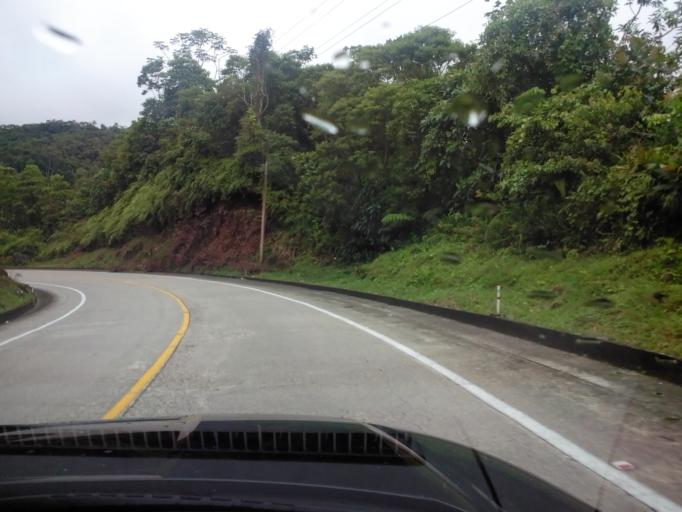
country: EC
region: Napo
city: Archidona
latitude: -0.7832
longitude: -77.7803
